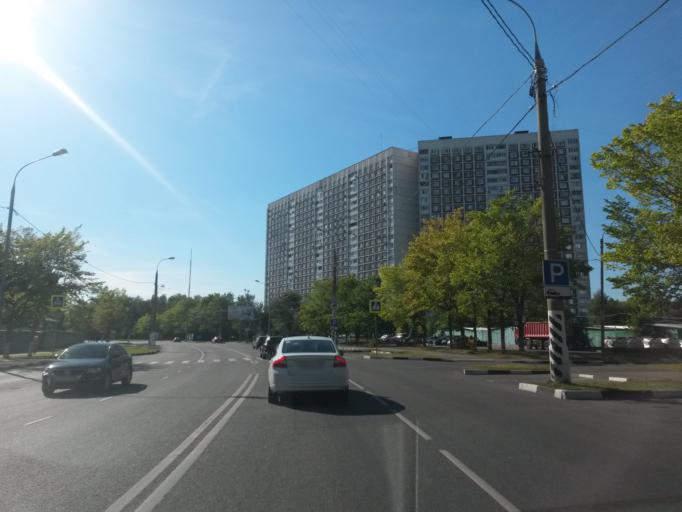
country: RU
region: Moscow
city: Yasenevo
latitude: 55.6134
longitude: 37.5344
